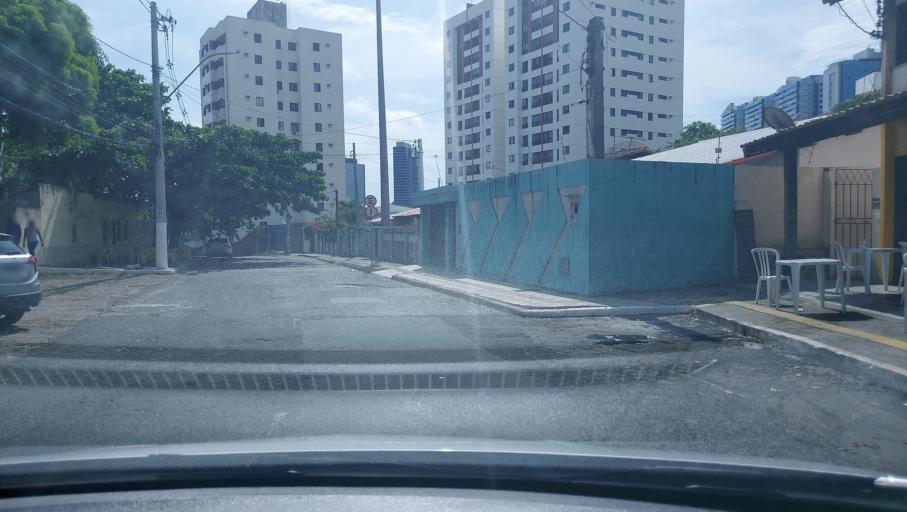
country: BR
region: Bahia
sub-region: Salvador
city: Salvador
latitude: -12.9825
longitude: -38.4476
